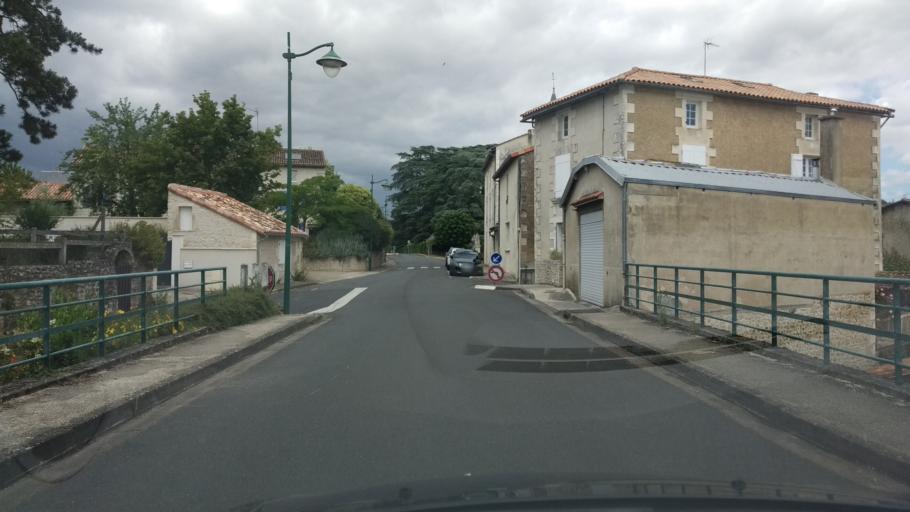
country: FR
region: Poitou-Charentes
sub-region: Departement de la Vienne
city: Vouneuil-sous-Biard
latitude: 46.5754
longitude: 0.2733
